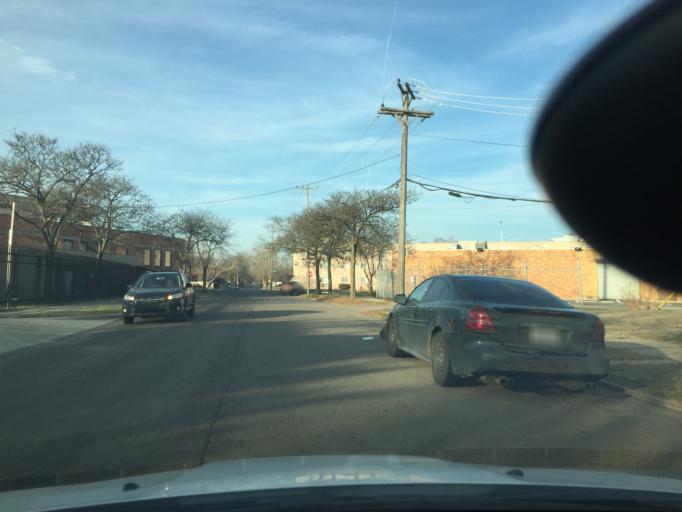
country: US
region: Michigan
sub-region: Macomb County
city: Eastpointe
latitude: 42.4444
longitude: -82.9704
